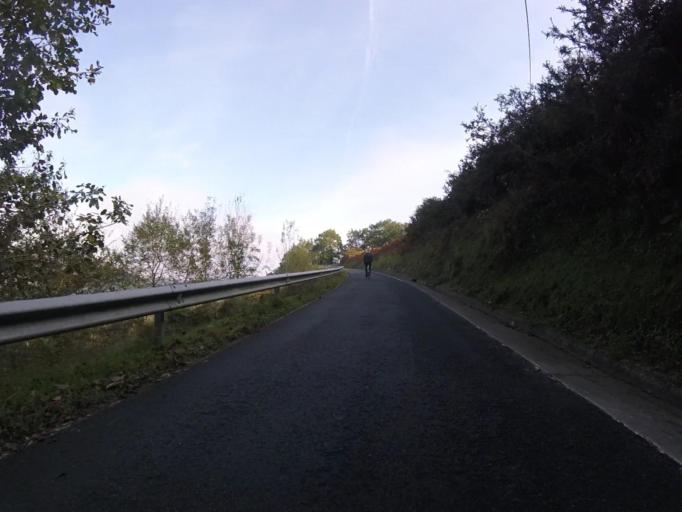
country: ES
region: Navarre
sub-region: Provincia de Navarra
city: Arano
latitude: 43.2052
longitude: -1.8863
